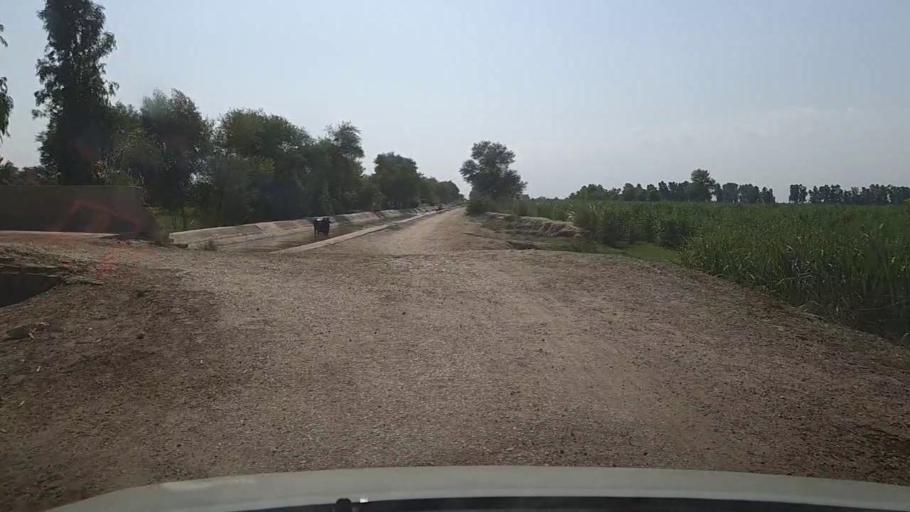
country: PK
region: Sindh
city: Mirpur Mathelo
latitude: 28.1177
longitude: 69.5891
